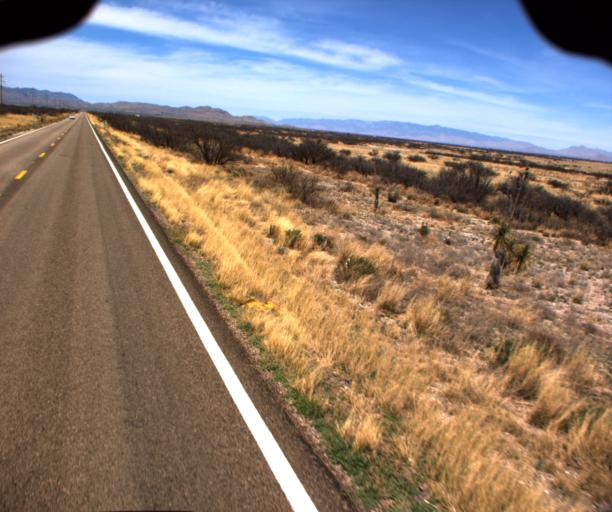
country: US
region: Arizona
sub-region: Cochise County
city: Willcox
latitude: 32.1509
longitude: -109.9364
